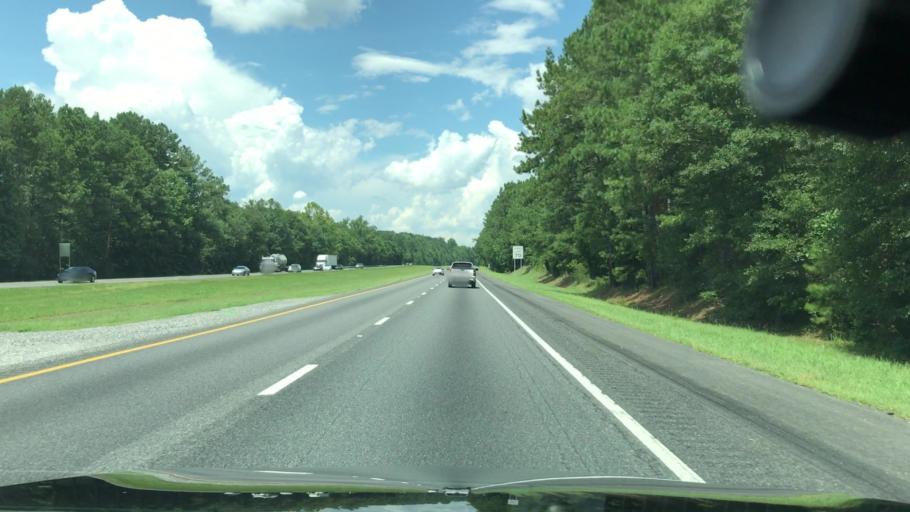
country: US
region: South Carolina
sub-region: York County
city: Lesslie
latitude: 34.8203
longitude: -81.0330
